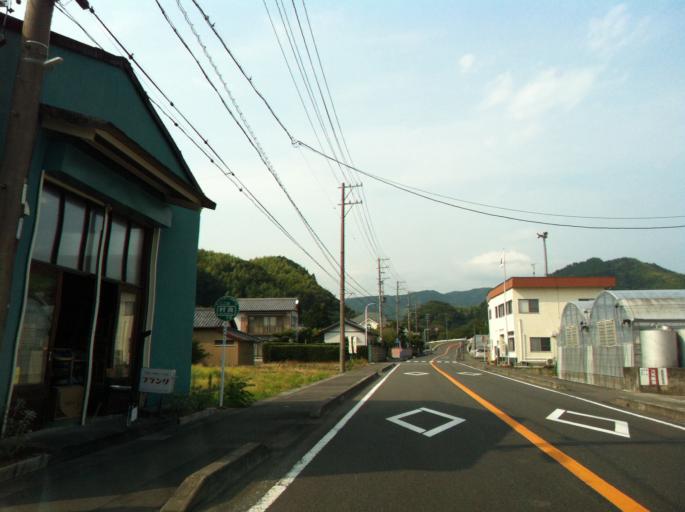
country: JP
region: Shizuoka
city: Fujieda
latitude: 34.9176
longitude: 138.2693
